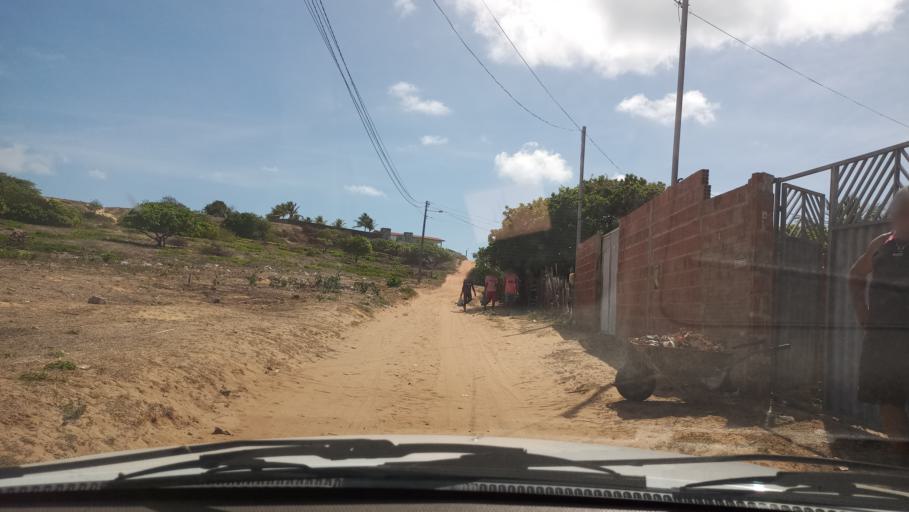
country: BR
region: Rio Grande do Norte
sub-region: Maxaranguape
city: Sao Miguel
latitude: -5.5131
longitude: -35.2647
